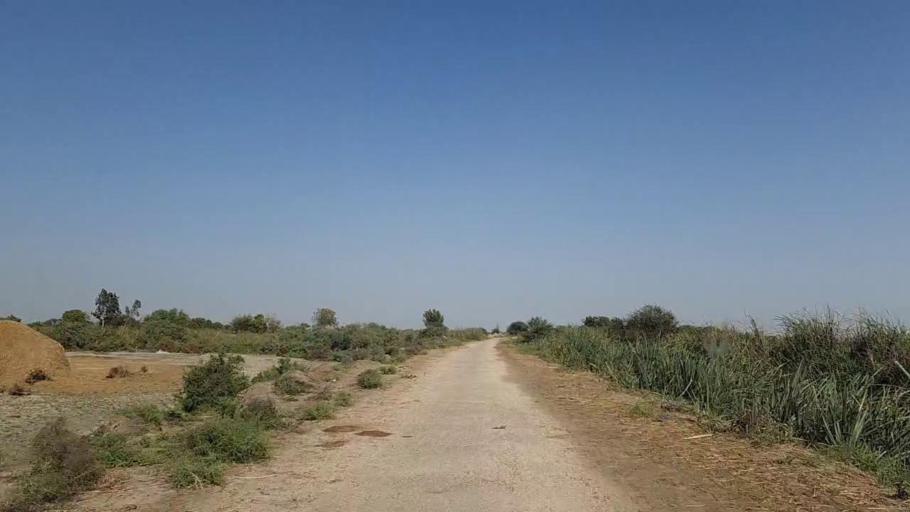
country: PK
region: Sindh
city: Chuhar Jamali
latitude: 24.4817
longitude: 68.1077
